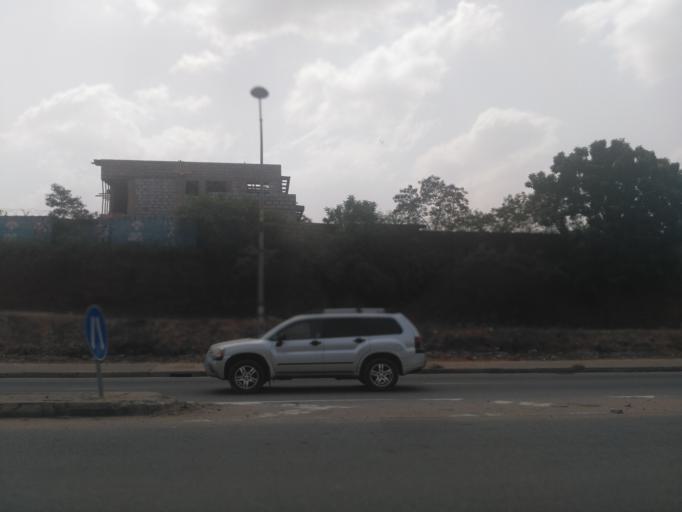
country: GH
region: Greater Accra
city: Dome
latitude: 5.6146
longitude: -0.2181
